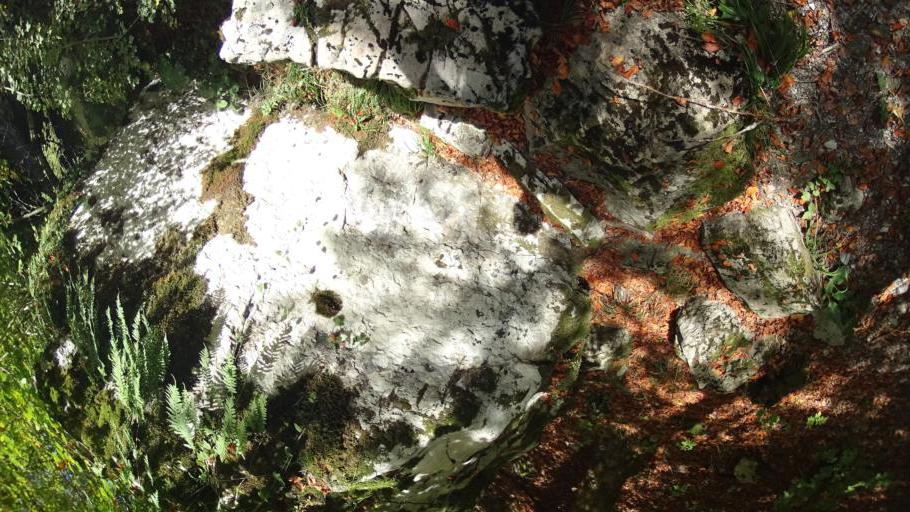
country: ES
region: Navarre
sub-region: Provincia de Navarra
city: Oronz
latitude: 42.9818
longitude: -1.1181
